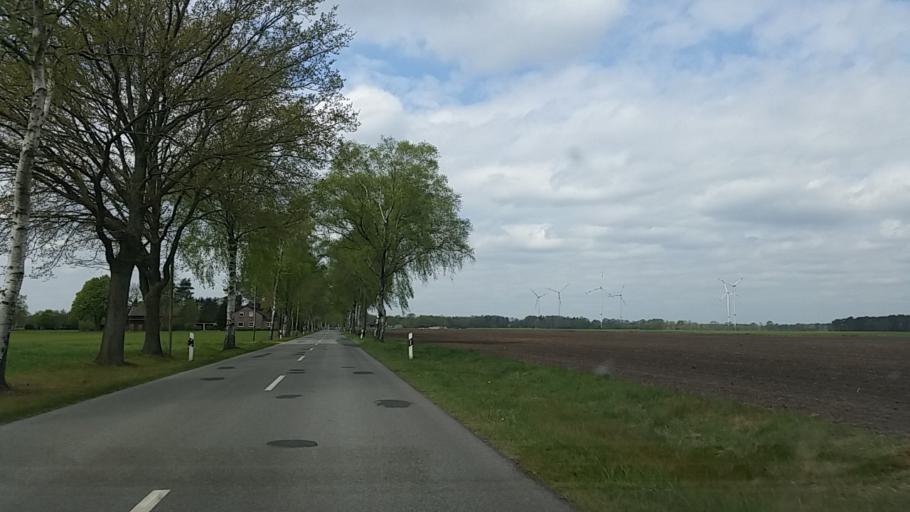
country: DE
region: Lower Saxony
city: Otter
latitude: 53.1942
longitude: 9.7245
